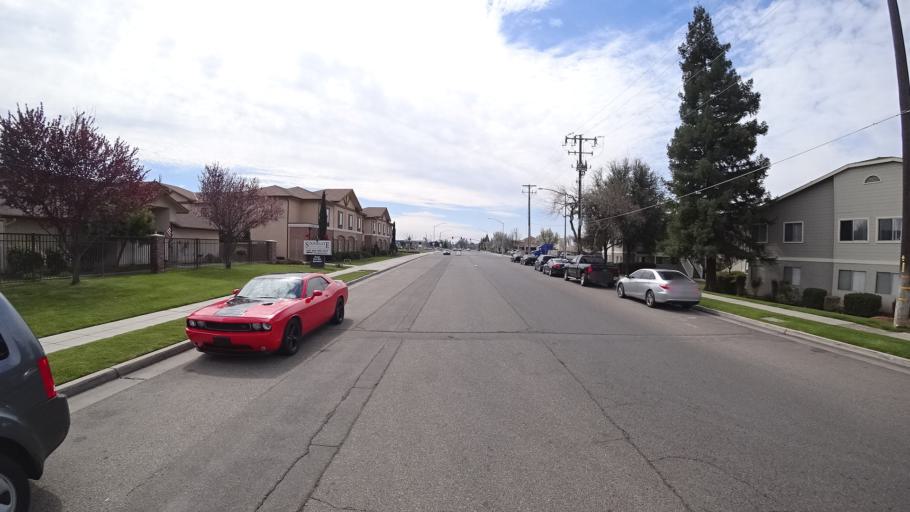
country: US
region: California
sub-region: Fresno County
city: West Park
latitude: 36.7954
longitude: -119.8714
